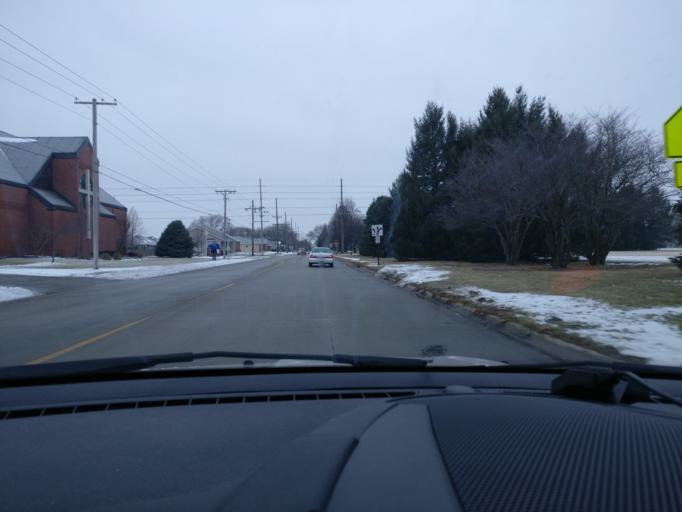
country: US
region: Nebraska
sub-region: Dodge County
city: Fremont
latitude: 41.4455
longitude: -96.4576
